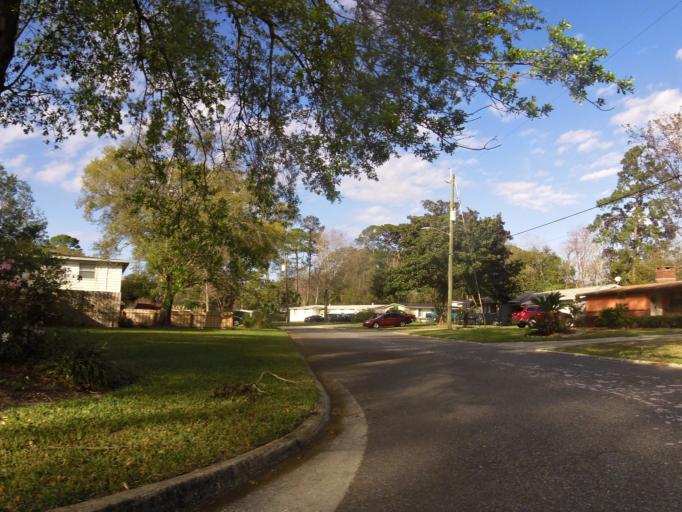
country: US
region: Florida
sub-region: Duval County
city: Jacksonville
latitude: 30.2811
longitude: -81.6132
